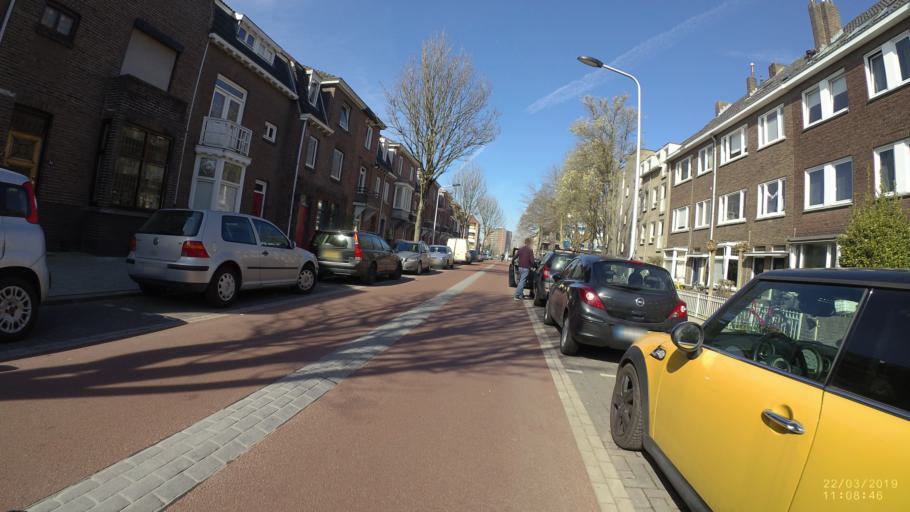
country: NL
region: Limburg
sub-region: Gemeente Maastricht
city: Maastricht
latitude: 50.8511
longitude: 5.6733
